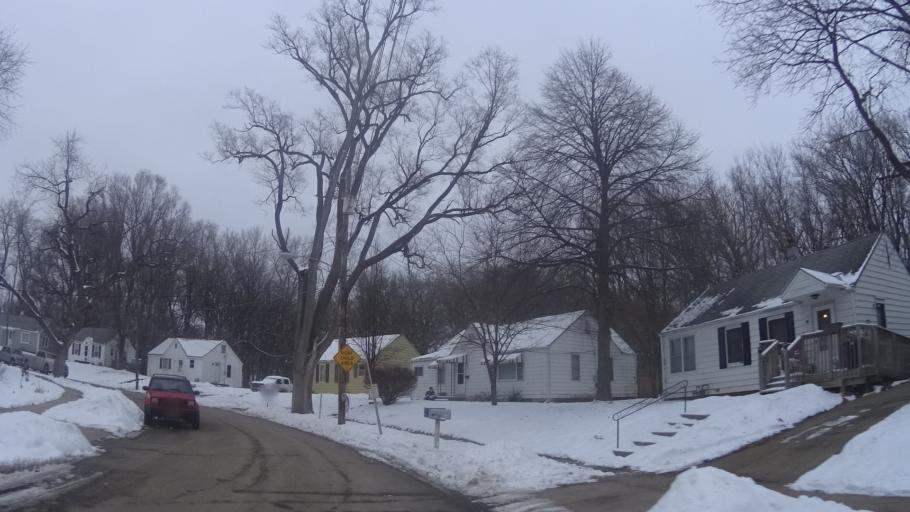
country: US
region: Nebraska
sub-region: Sarpy County
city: Offutt Air Force Base
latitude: 41.1363
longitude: -95.9222
